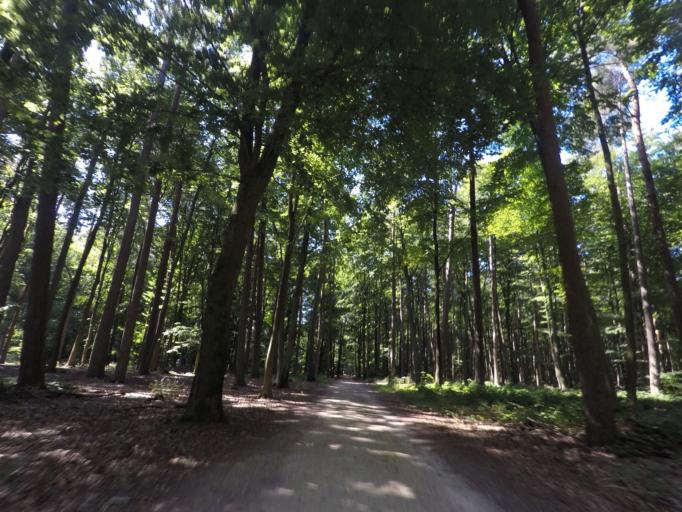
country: LU
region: Luxembourg
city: Bereldange
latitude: 49.6448
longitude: 6.1062
